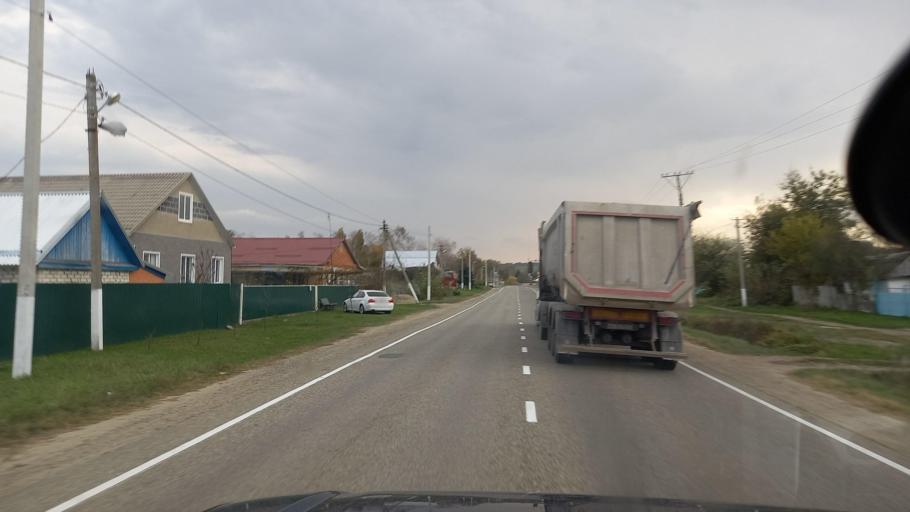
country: RU
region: Krasnodarskiy
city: Mostovskoy
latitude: 44.3838
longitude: 40.7405
